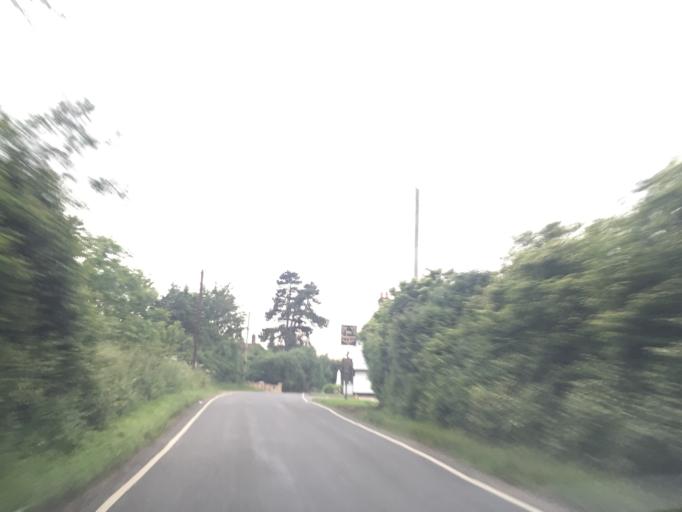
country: GB
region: England
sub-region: Hertfordshire
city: Sawbridgeworth
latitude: 51.7615
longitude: 0.1741
